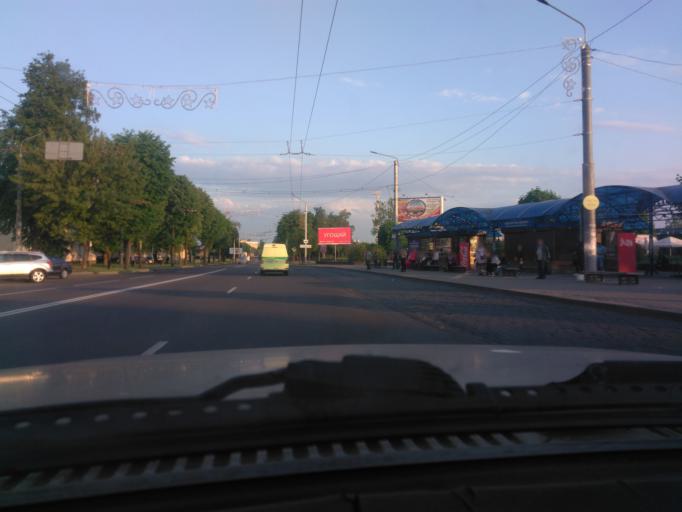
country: BY
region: Mogilev
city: Mahilyow
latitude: 53.9259
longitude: 30.3402
